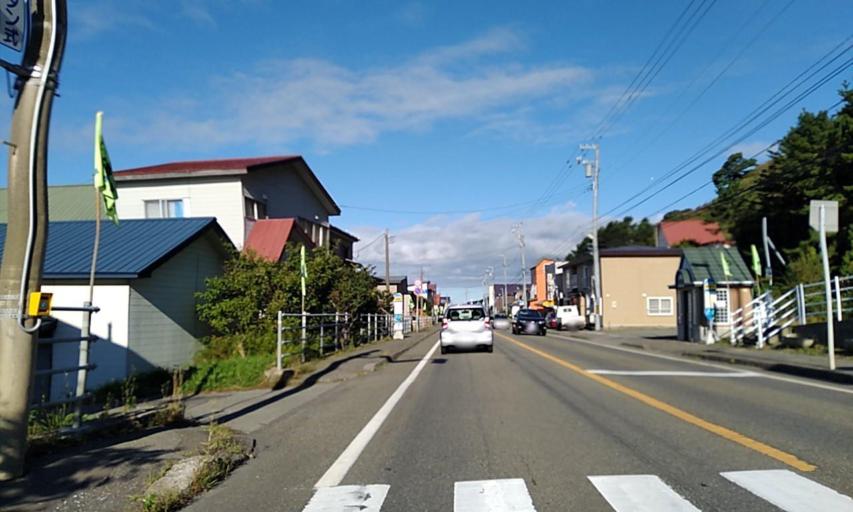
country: JP
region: Hokkaido
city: Shizunai-furukawacho
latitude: 42.1779
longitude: 142.7343
